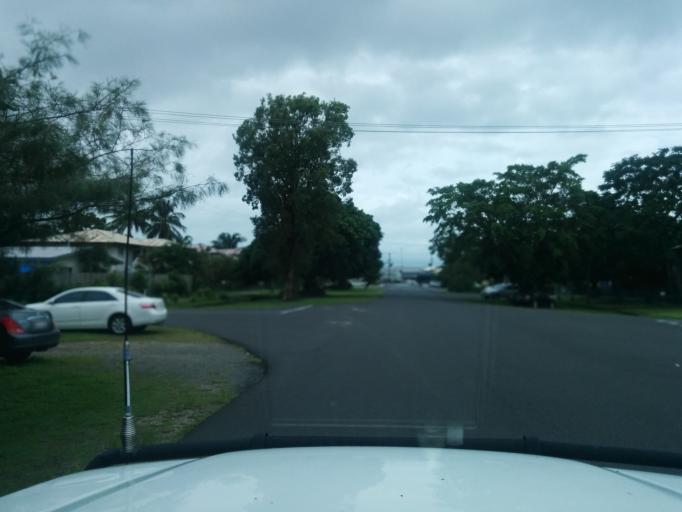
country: AU
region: Queensland
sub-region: Cairns
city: Cairns
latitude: -16.9307
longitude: 145.7560
